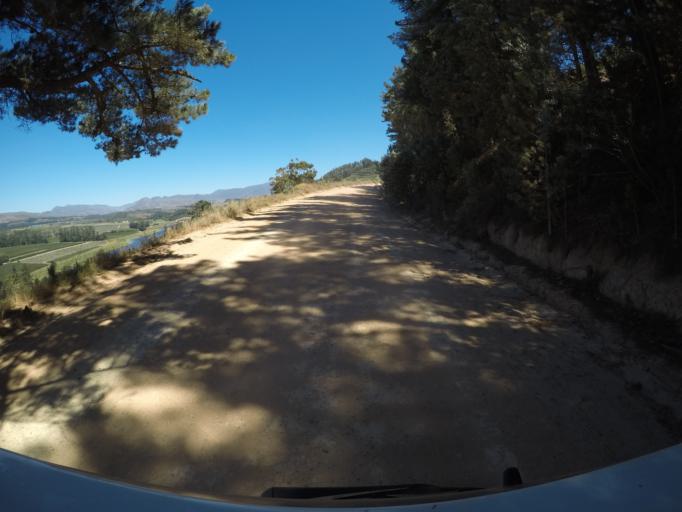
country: ZA
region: Western Cape
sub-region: Overberg District Municipality
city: Grabouw
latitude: -34.2424
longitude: 19.0872
